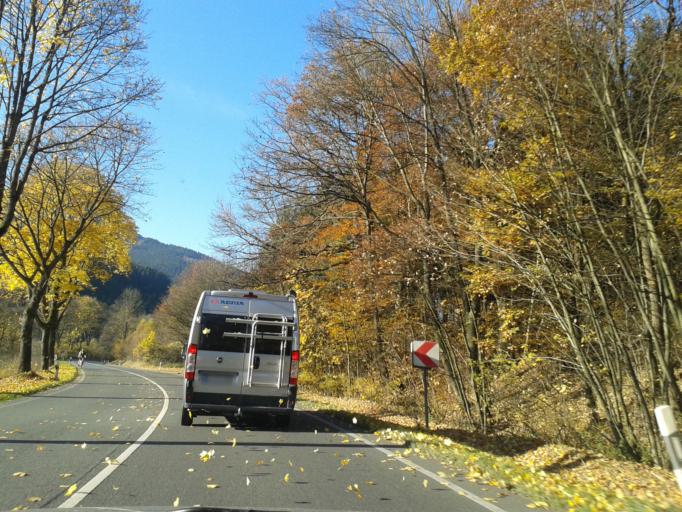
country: DE
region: North Rhine-Westphalia
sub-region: Regierungsbezirk Arnsberg
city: Olsberg
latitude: 51.3225
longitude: 8.4986
